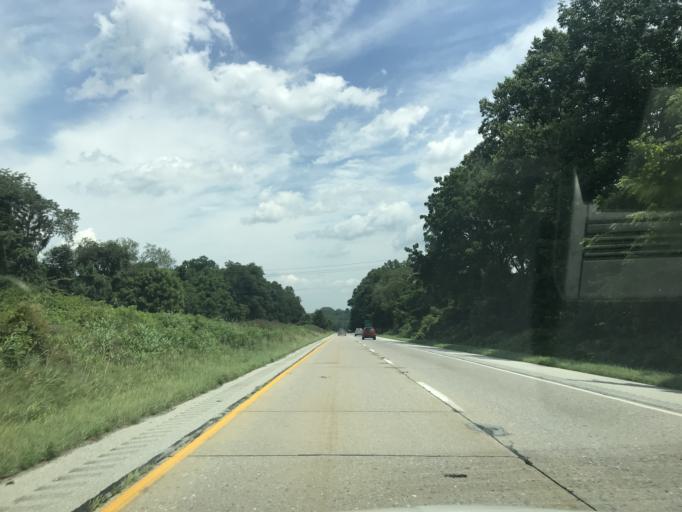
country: US
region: Pennsylvania
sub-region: Chester County
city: Toughkenamon
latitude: 39.8520
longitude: -75.7400
